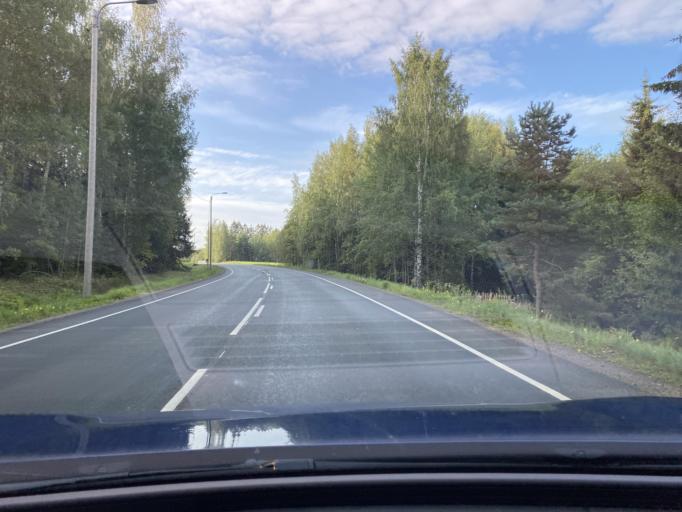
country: FI
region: Kymenlaakso
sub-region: Kouvola
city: Kouvola
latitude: 60.8828
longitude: 26.6014
